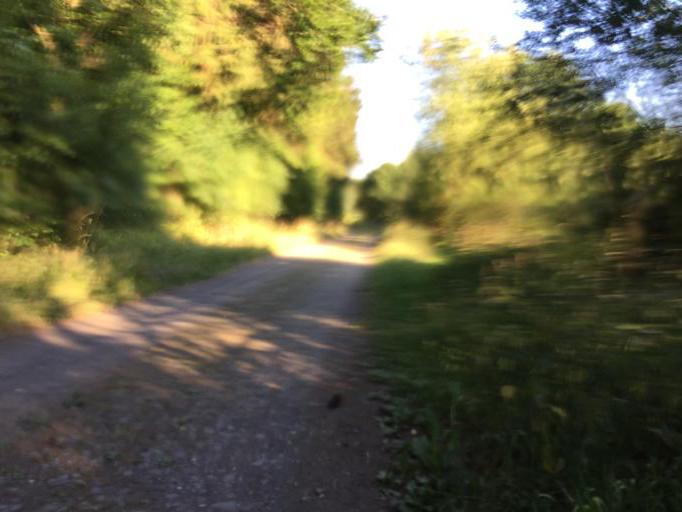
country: DE
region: Rheinland-Pfalz
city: Berod bei Wallmerod
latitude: 50.4906
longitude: 7.9327
